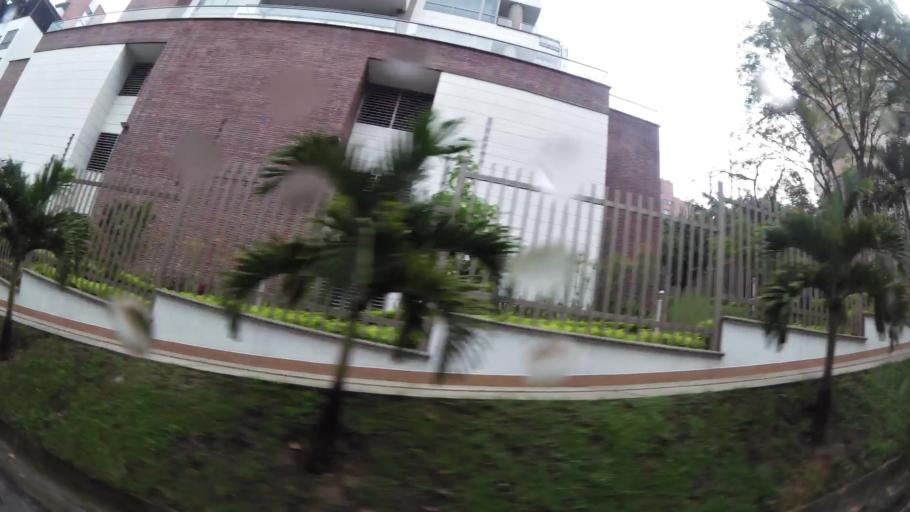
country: CO
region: Antioquia
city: Envigado
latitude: 6.1983
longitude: -75.5707
